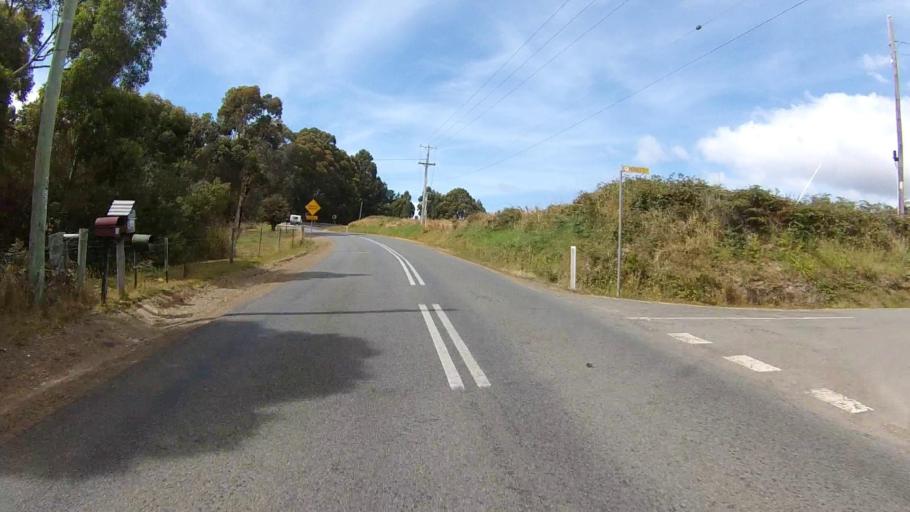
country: AU
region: Tasmania
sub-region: Kingborough
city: Kettering
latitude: -43.2103
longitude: 147.2560
